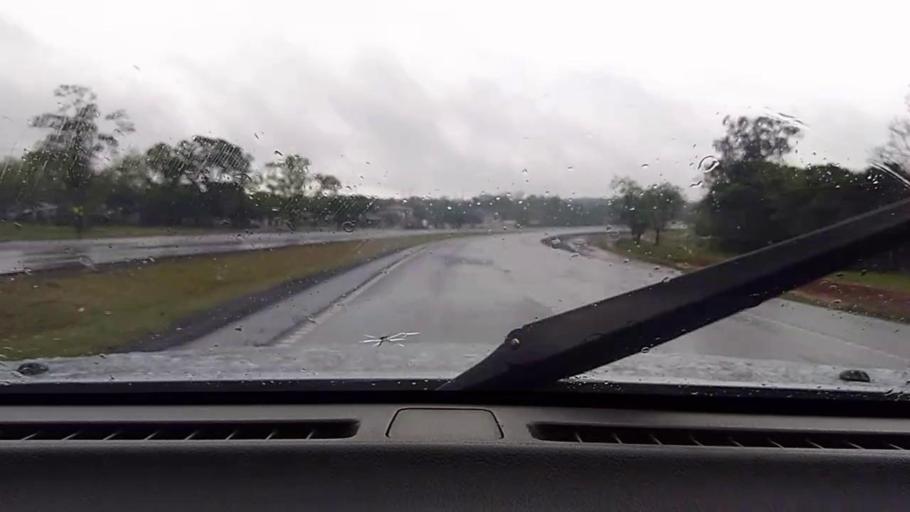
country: PY
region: Caaguazu
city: Repatriacion
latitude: -25.4655
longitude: -55.9330
